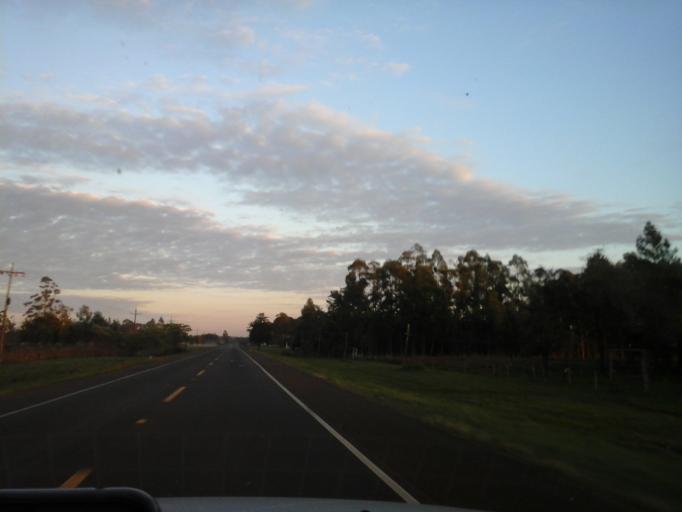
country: PY
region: Itapua
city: General Delgado
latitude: -27.0743
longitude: -56.5905
